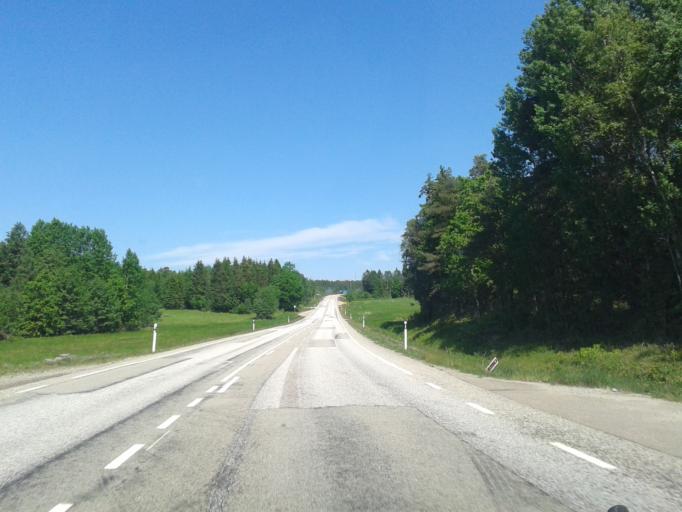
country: SE
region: Vaestra Goetaland
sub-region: Stromstads Kommun
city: Stroemstad
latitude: 58.8720
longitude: 11.2707
